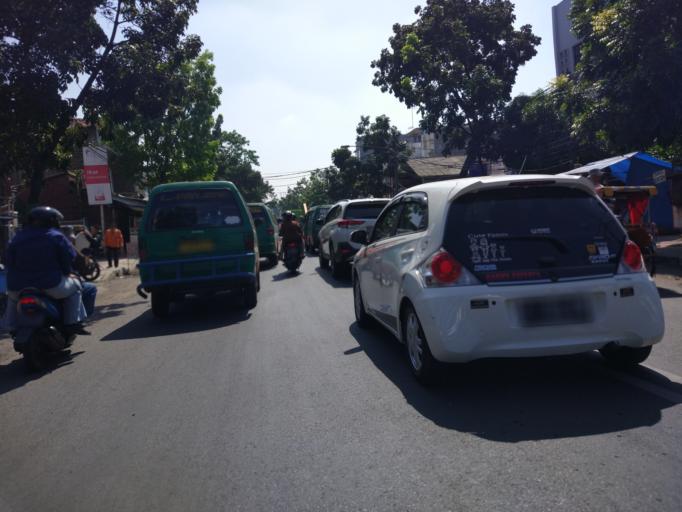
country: ID
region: West Java
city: Bandung
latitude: -6.9309
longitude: 107.5970
